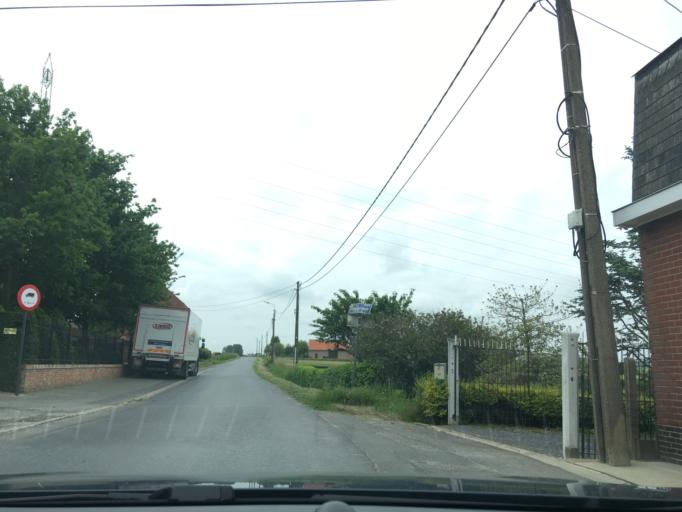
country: BE
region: Flanders
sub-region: Provincie West-Vlaanderen
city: Moorslede
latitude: 50.8464
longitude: 3.0725
